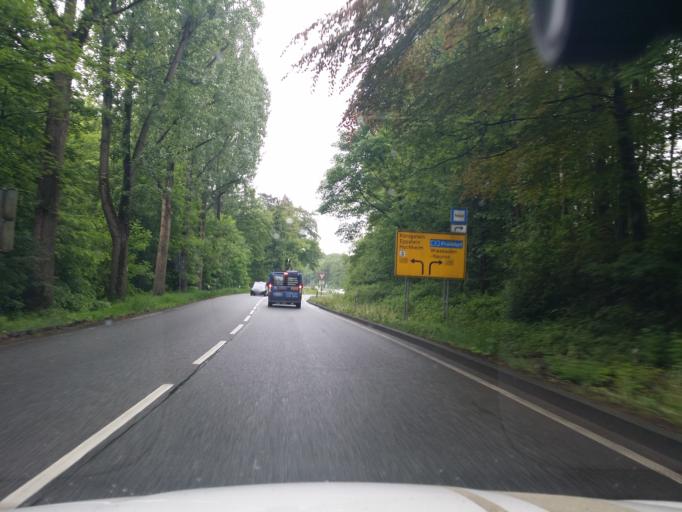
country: DE
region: Hesse
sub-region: Regierungsbezirk Darmstadt
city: Niedernhausen
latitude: 50.1438
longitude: 8.3286
